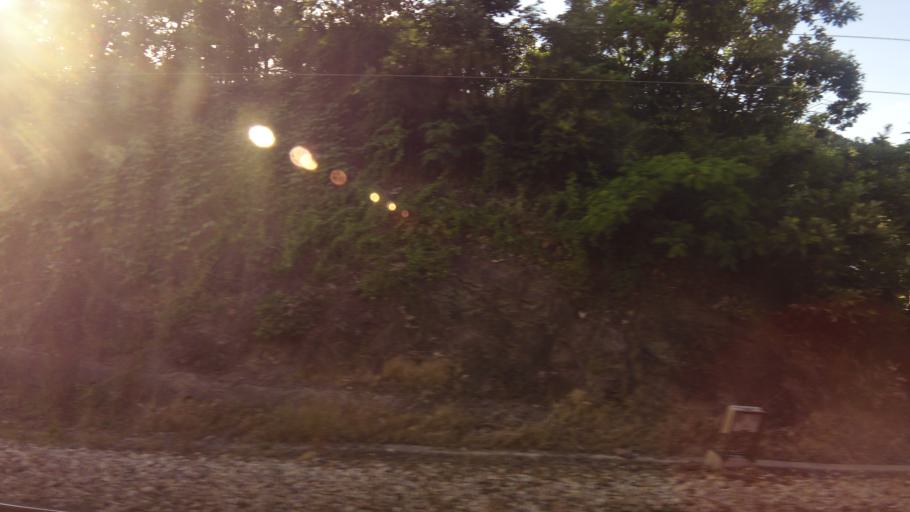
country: KR
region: Chungcheongbuk-do
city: Yong-dong
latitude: 36.1670
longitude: 127.8123
